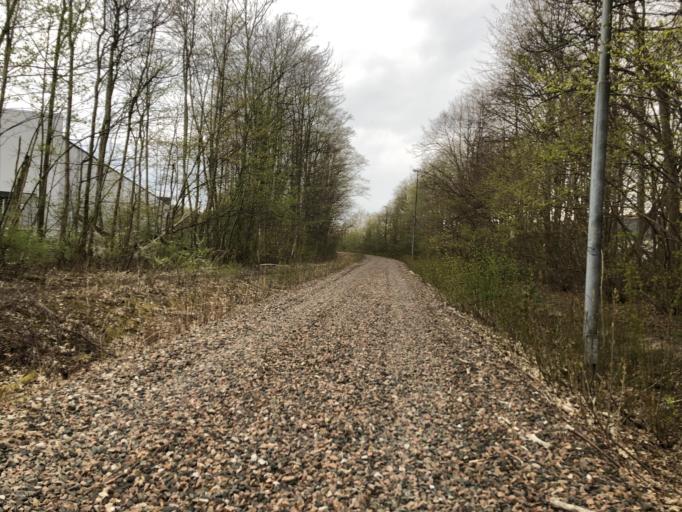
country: SE
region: Skane
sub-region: Malmo
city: Tygelsjo
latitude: 55.5532
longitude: 13.0435
